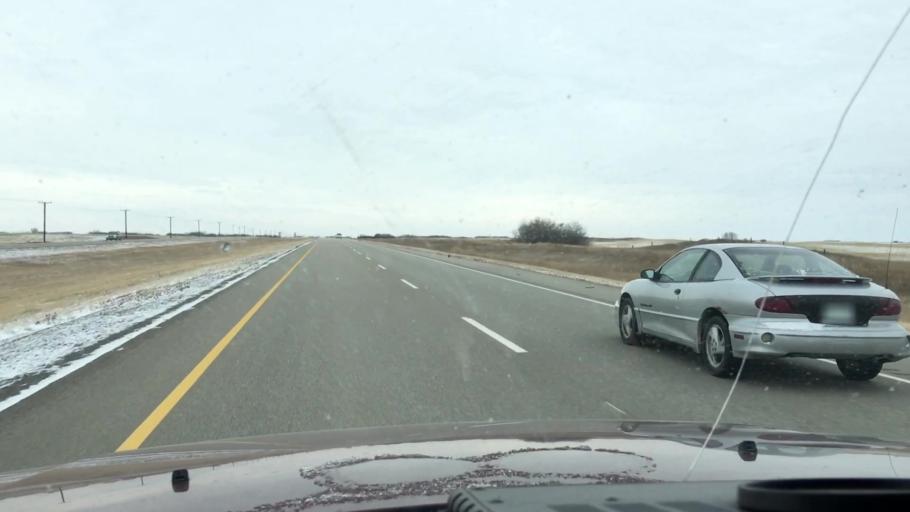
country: CA
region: Saskatchewan
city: Watrous
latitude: 51.4054
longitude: -106.1811
